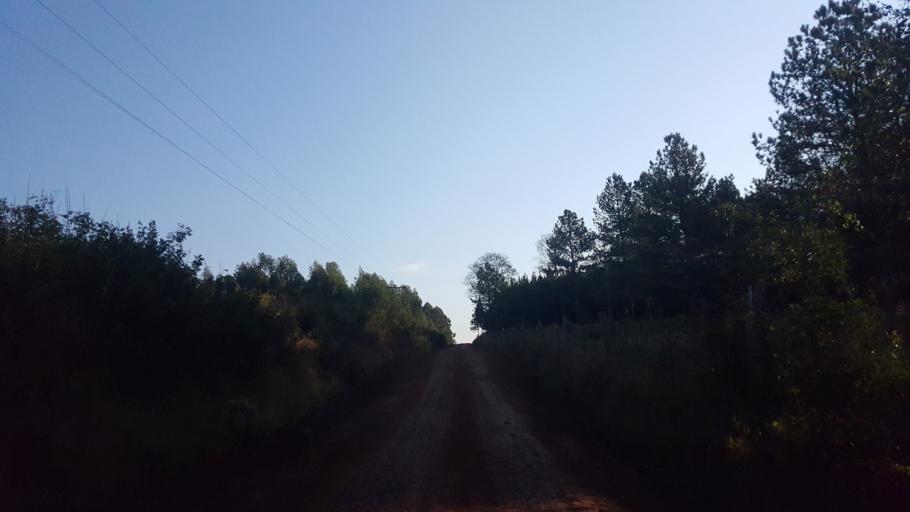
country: AR
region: Misiones
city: Capiovi
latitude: -26.9187
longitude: -55.0517
